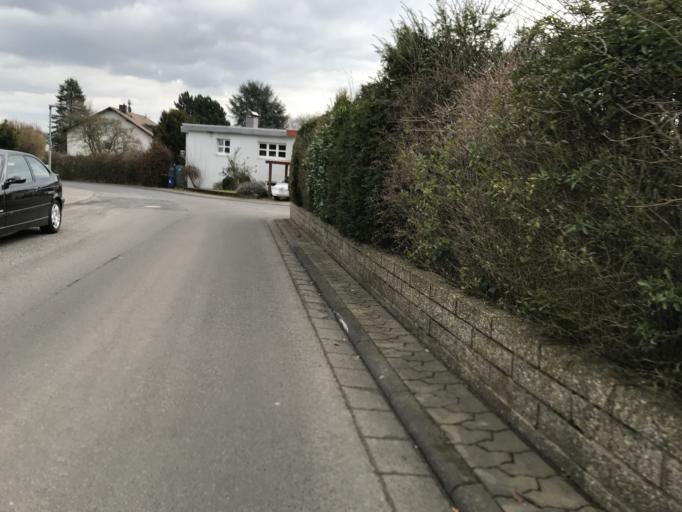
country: DE
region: Hesse
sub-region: Regierungsbezirk Giessen
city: Lich
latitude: 50.5269
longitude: 8.8114
